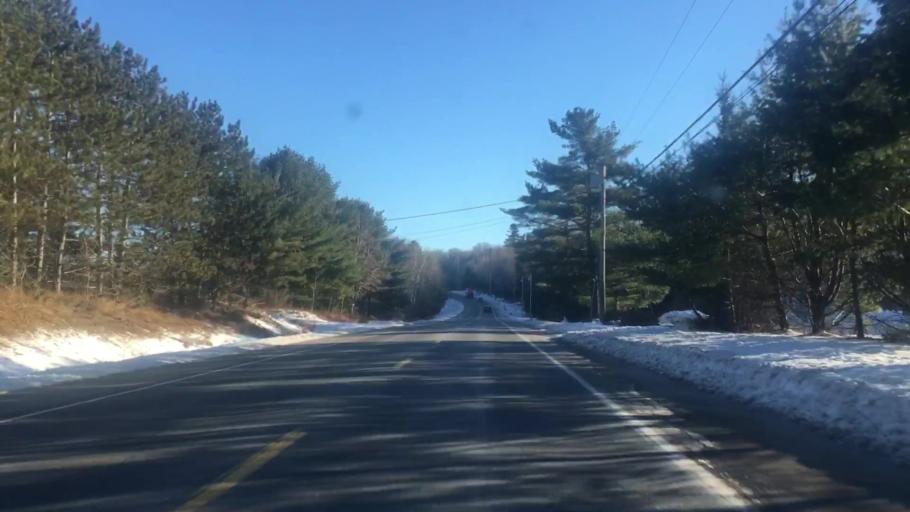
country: US
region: Maine
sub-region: Somerset County
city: Norridgewock
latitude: 44.6736
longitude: -69.7190
